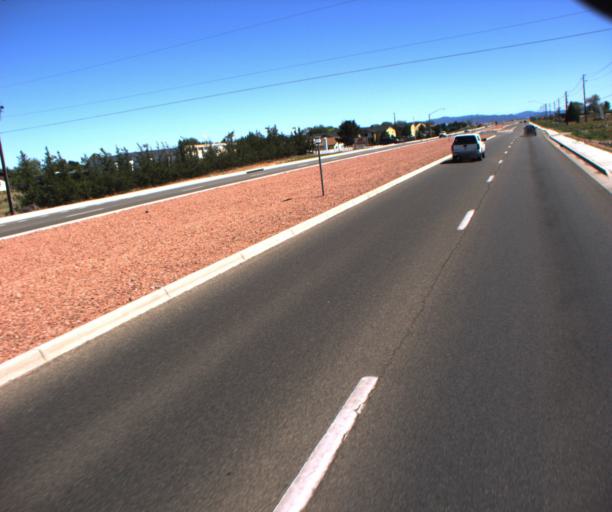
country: US
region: Arizona
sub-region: Yavapai County
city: Chino Valley
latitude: 34.7261
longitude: -112.4540
